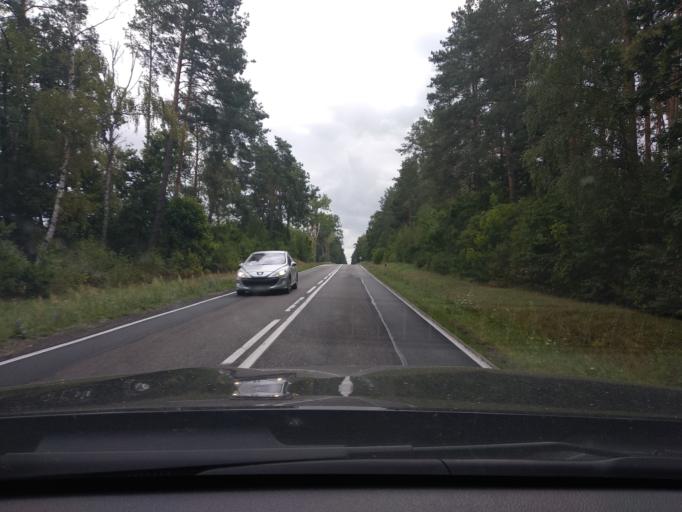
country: PL
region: Masovian Voivodeship
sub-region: Powiat pultuski
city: Obryte
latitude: 52.6430
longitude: 21.2669
